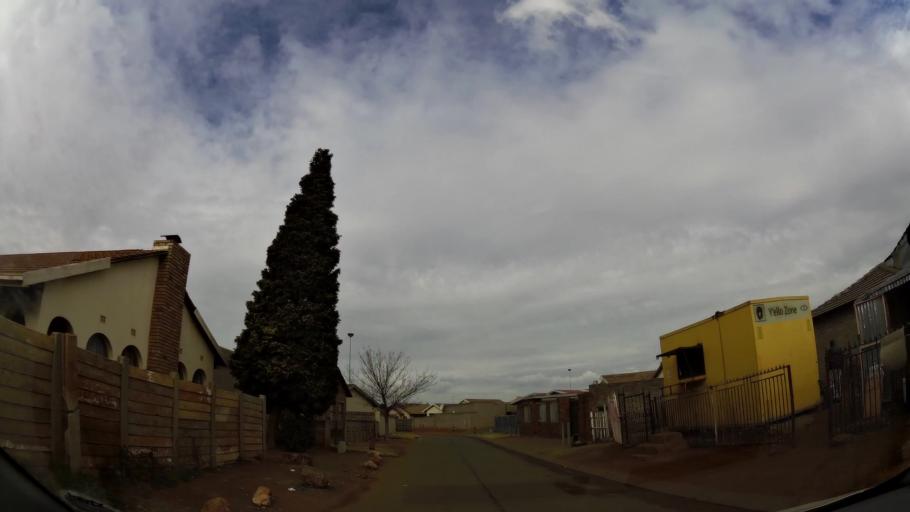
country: ZA
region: Gauteng
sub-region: Ekurhuleni Metropolitan Municipality
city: Germiston
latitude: -26.3755
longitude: 28.1557
